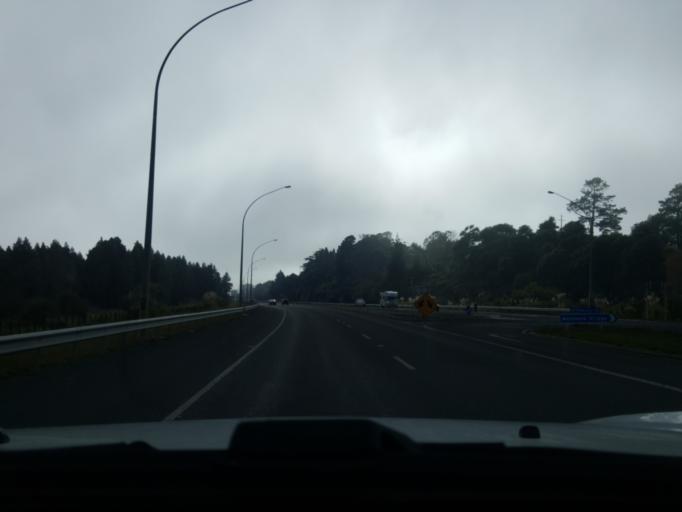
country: NZ
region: Waikato
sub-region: Waikato District
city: Te Kauwhata
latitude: -37.3266
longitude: 175.0658
